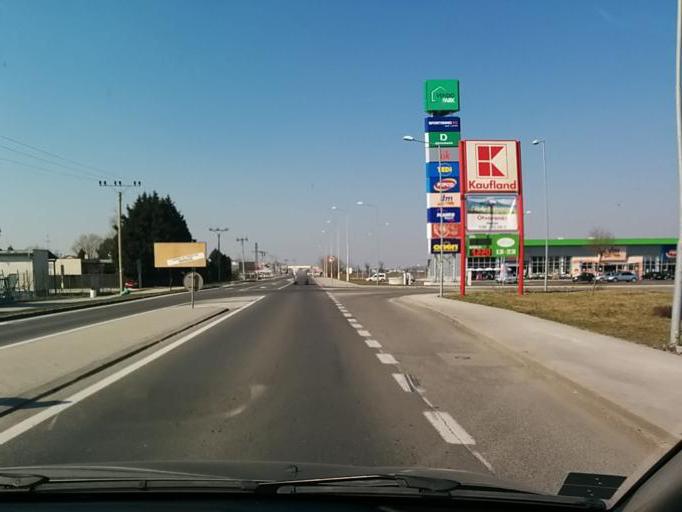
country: SK
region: Trnavsky
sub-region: Okres Galanta
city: Galanta
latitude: 48.1996
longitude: 17.7323
